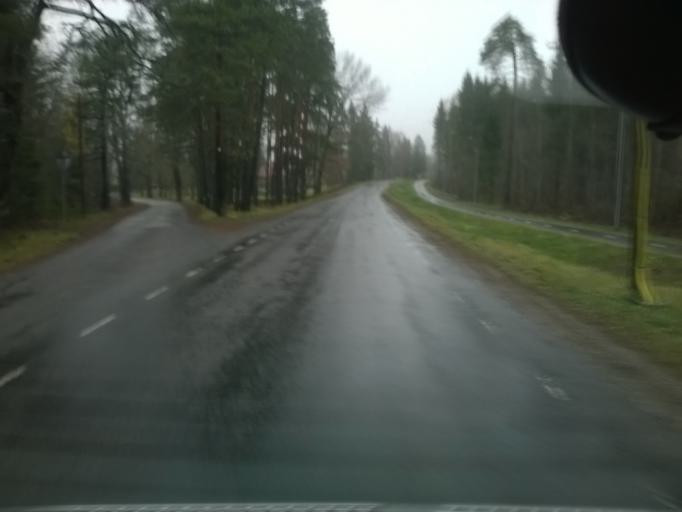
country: EE
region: Raplamaa
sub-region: Kohila vald
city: Kohila
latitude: 59.1701
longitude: 24.6532
